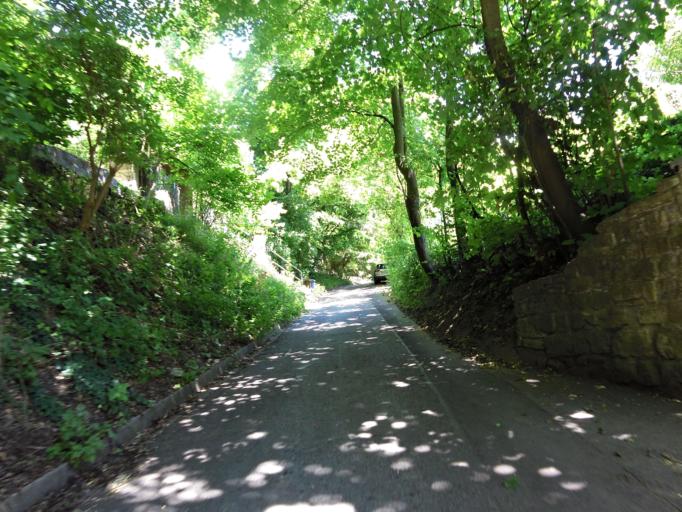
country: DE
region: Bavaria
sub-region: Regierungsbezirk Unterfranken
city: Wuerzburg
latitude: 49.8070
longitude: 9.9421
